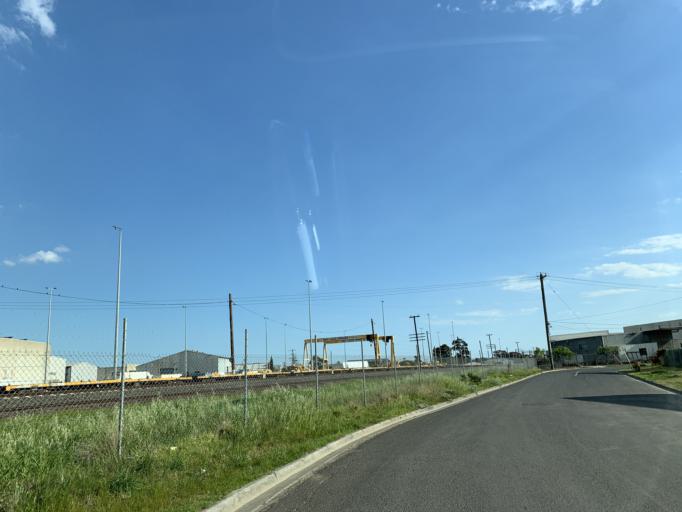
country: AU
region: Victoria
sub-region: Brimbank
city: Albion
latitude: -37.7597
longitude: 144.8344
